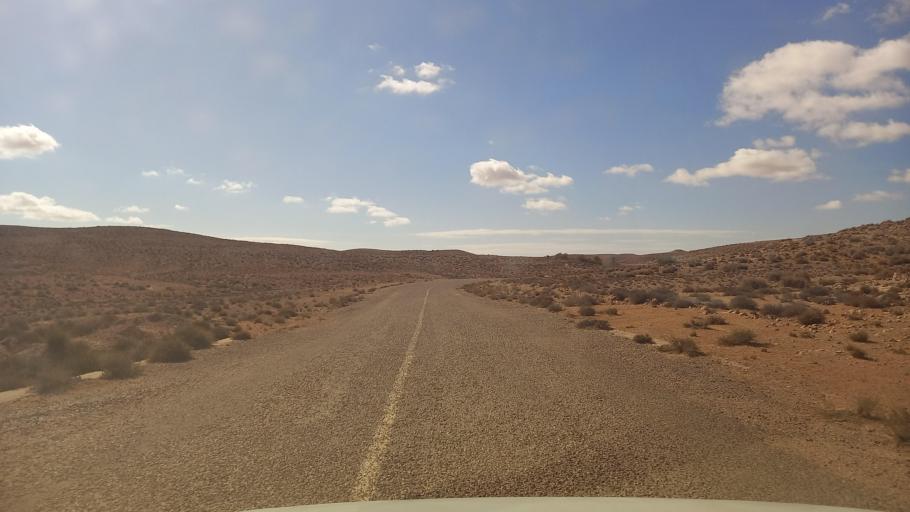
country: TN
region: Tataouine
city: Tataouine
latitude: 32.8783
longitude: 10.2400
